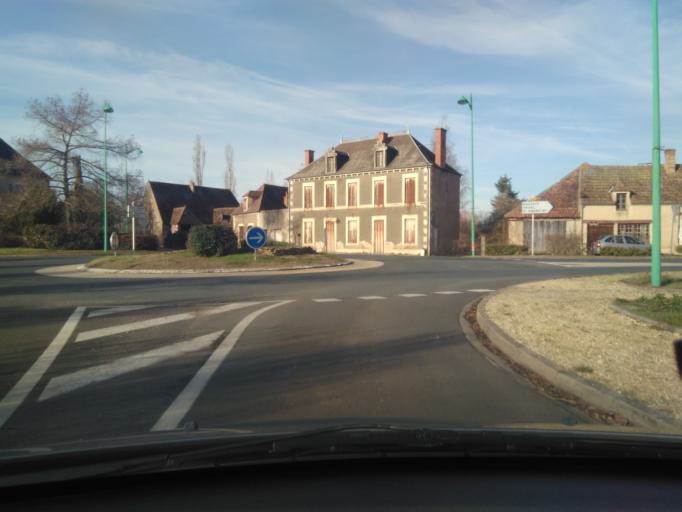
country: FR
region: Centre
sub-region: Departement du Cher
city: Orval
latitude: 46.6554
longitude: 2.4379
